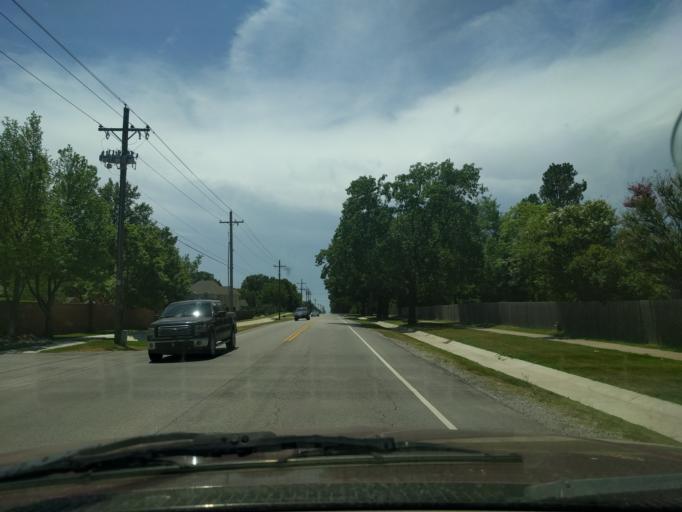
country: US
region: Oklahoma
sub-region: Tulsa County
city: Jenks
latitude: 36.0122
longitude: -95.9222
